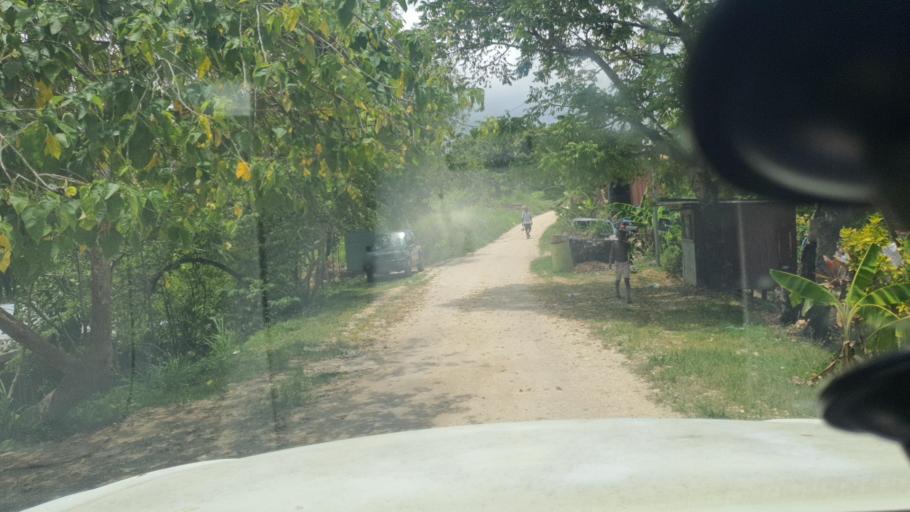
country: SB
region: Guadalcanal
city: Honiara
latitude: -9.4395
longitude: 159.9438
